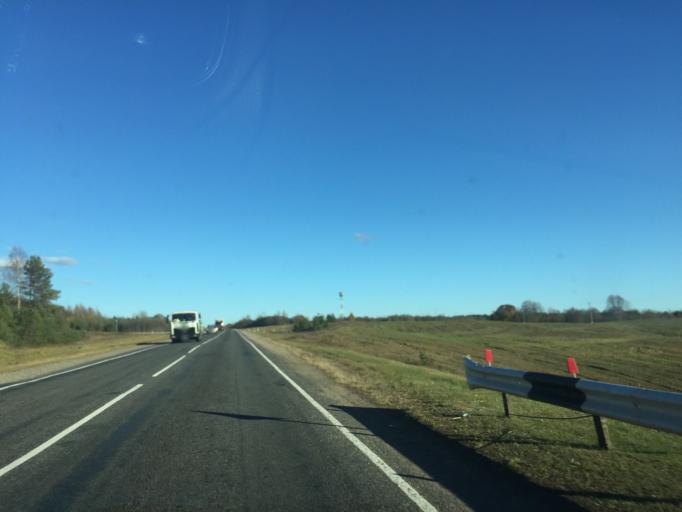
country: BY
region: Vitebsk
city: Dzisna
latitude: 55.2394
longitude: 28.0542
